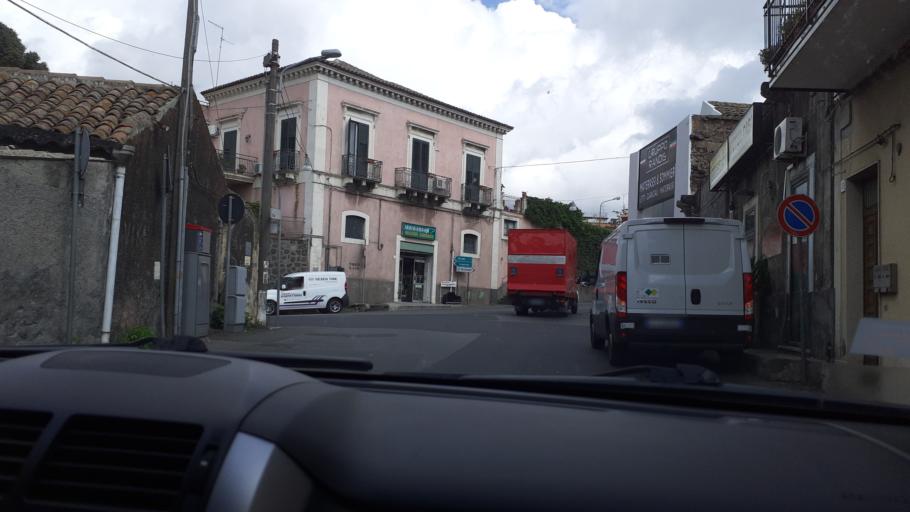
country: IT
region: Sicily
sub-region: Catania
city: San Gregorio di Catania
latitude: 37.5635
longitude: 15.1063
